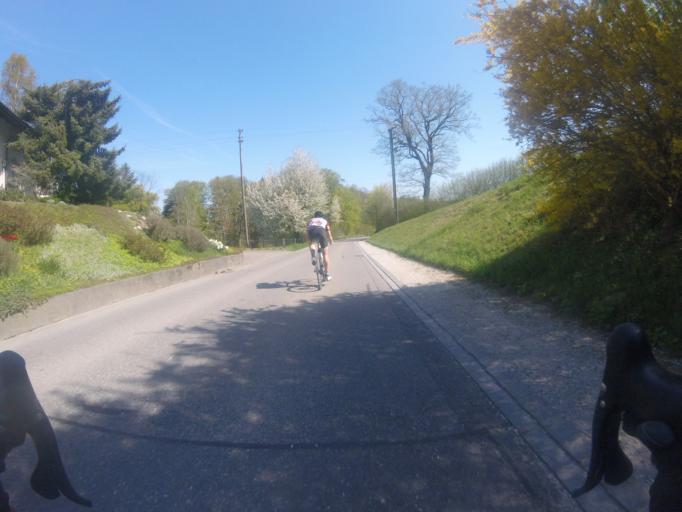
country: CH
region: Bern
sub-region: Bern-Mittelland District
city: Laupen
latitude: 46.9140
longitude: 7.2300
